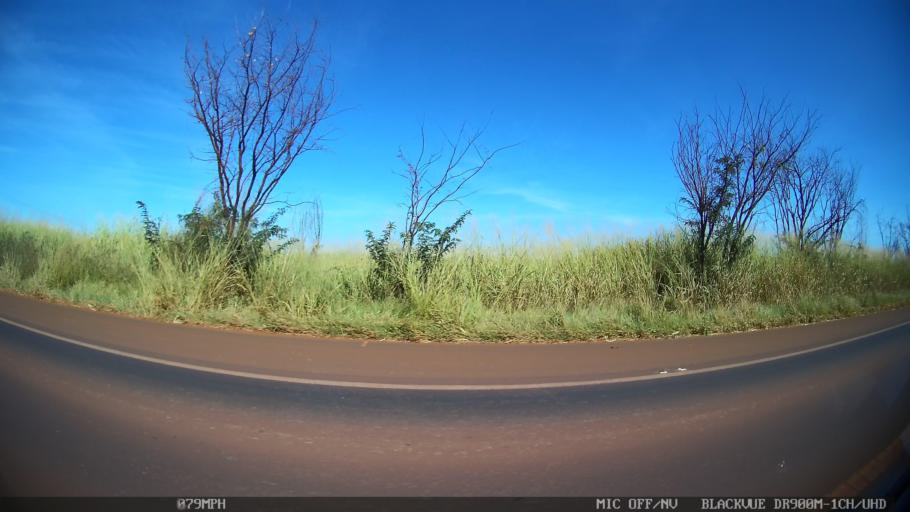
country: BR
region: Sao Paulo
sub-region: Sao Joaquim Da Barra
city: Sao Joaquim da Barra
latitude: -20.5444
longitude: -47.7854
